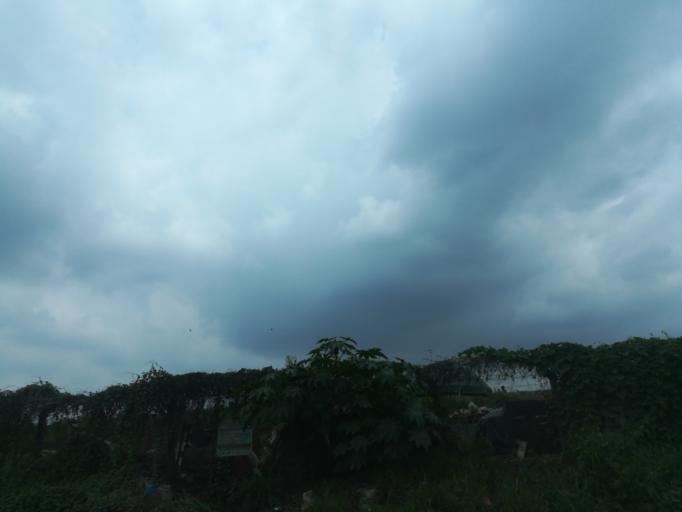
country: NG
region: Lagos
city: Agege
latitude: 6.6174
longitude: 3.3267
